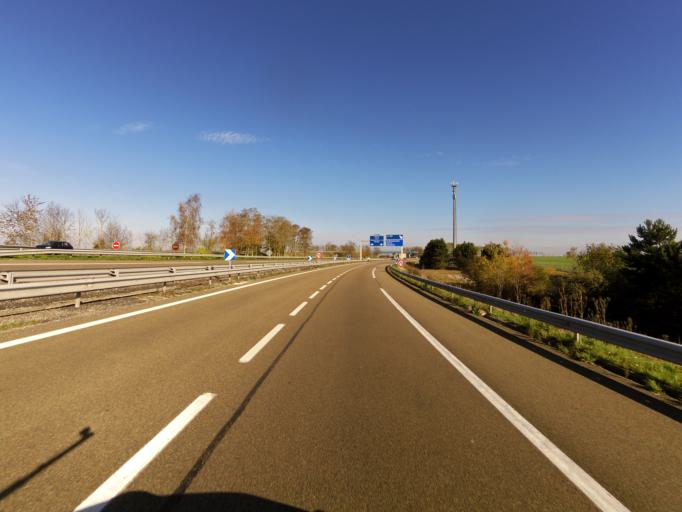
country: FR
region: Champagne-Ardenne
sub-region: Departement de la Marne
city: Fagnieres
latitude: 49.0508
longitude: 4.2834
